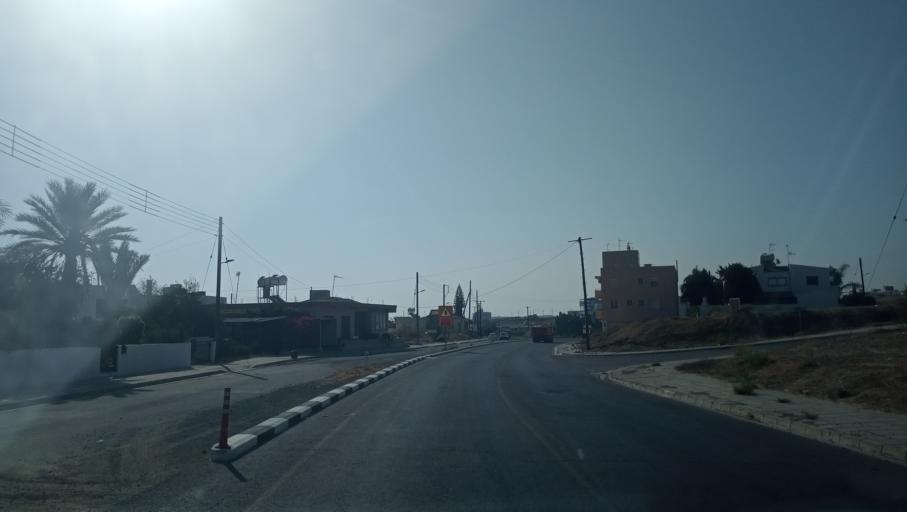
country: CY
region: Lefkosia
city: Geri
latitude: 35.1172
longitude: 33.4186
